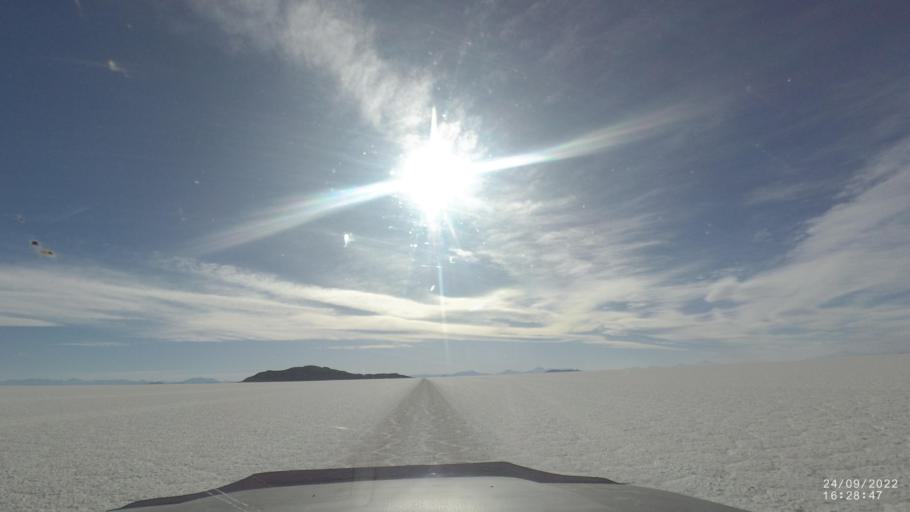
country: BO
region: Potosi
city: Colchani
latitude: -20.2413
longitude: -67.6051
